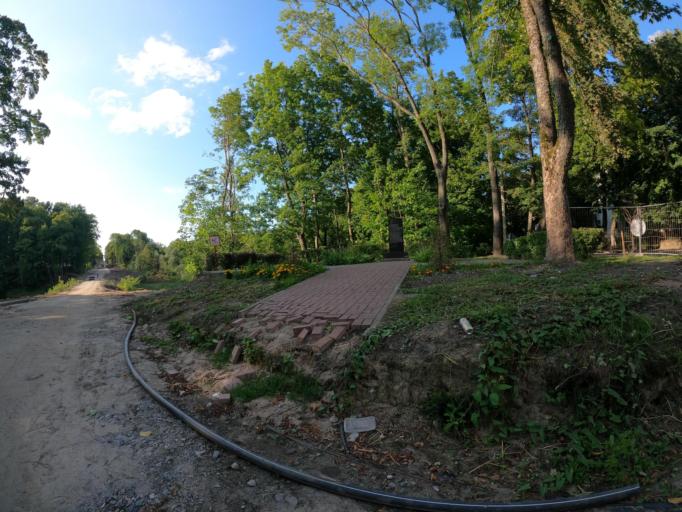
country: RU
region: Kaliningrad
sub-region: Gorod Kaliningrad
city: Kaliningrad
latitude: 54.7233
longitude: 20.4572
